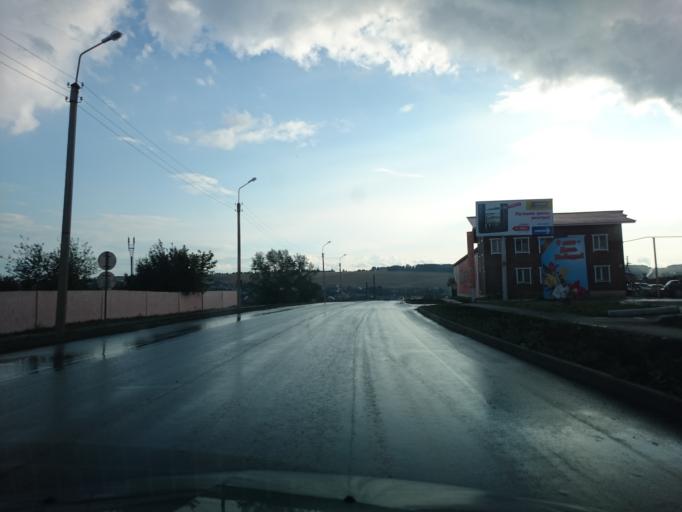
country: RU
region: Bashkortostan
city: Beloretsk
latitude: 53.9569
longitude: 58.3606
